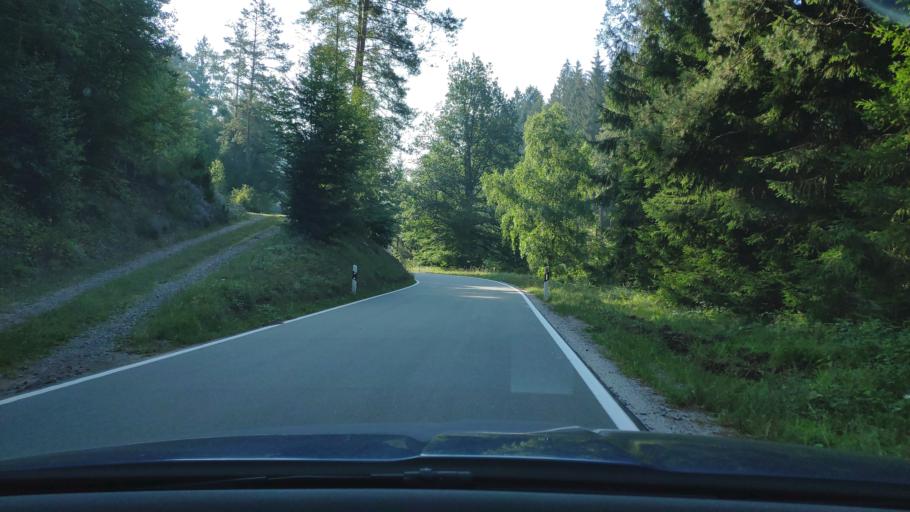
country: DE
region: Rheinland-Pfalz
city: Ludwigswinkel
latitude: 49.1036
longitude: 7.6199
